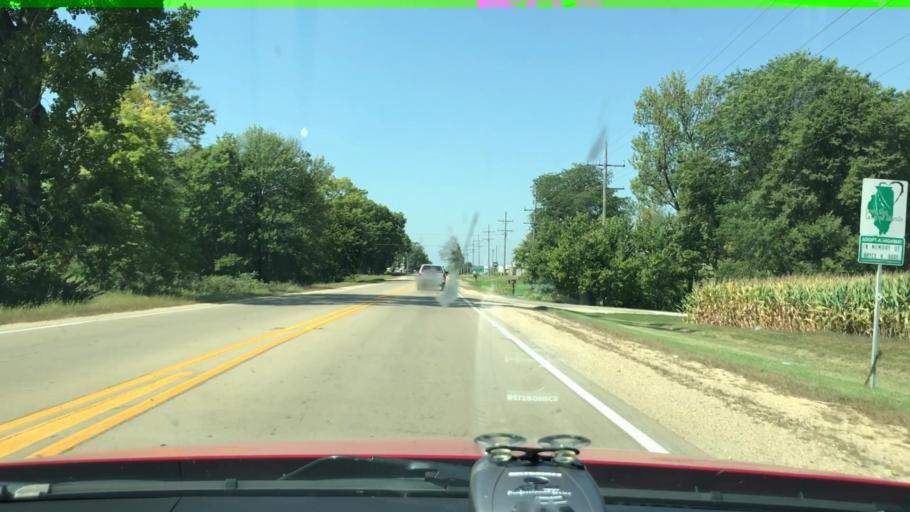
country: US
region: Illinois
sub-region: Whiteside County
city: Sterling
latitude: 41.7724
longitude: -89.7212
